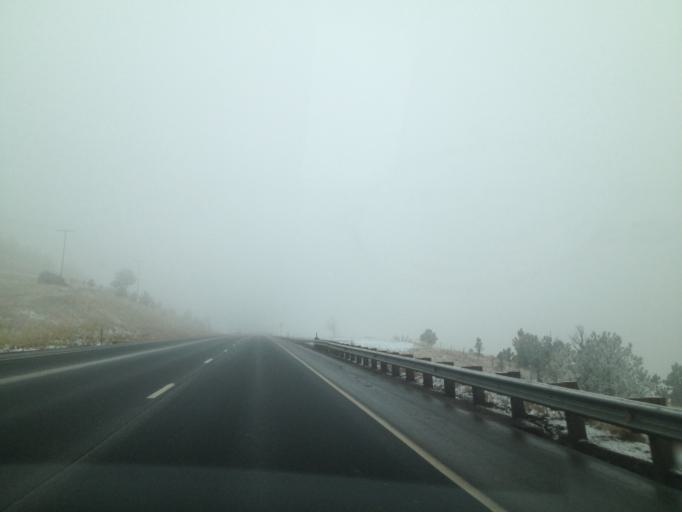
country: US
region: Colorado
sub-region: Boulder County
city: Superior
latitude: 39.9402
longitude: -105.2360
